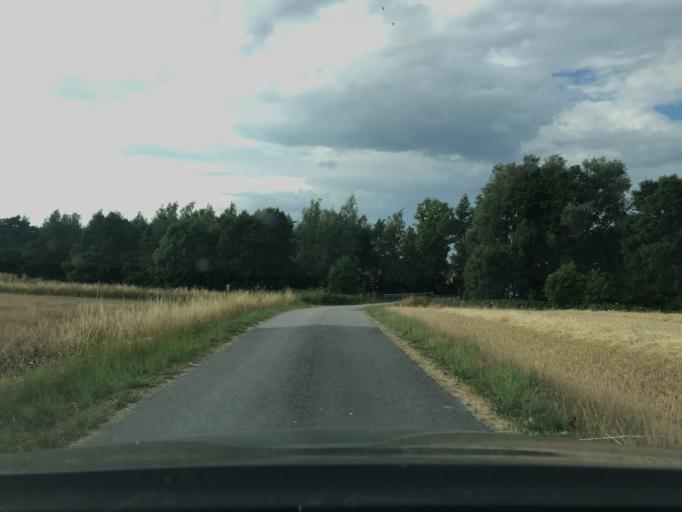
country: SE
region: Skane
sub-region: Simrishamns Kommun
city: Kivik
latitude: 55.5405
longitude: 14.1526
